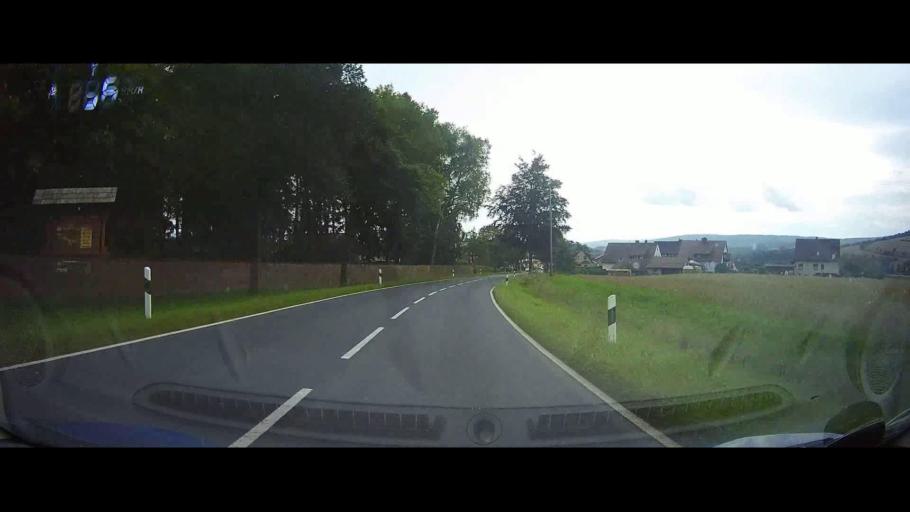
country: DE
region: Lower Saxony
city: Uslar
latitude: 51.6828
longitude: 9.6419
